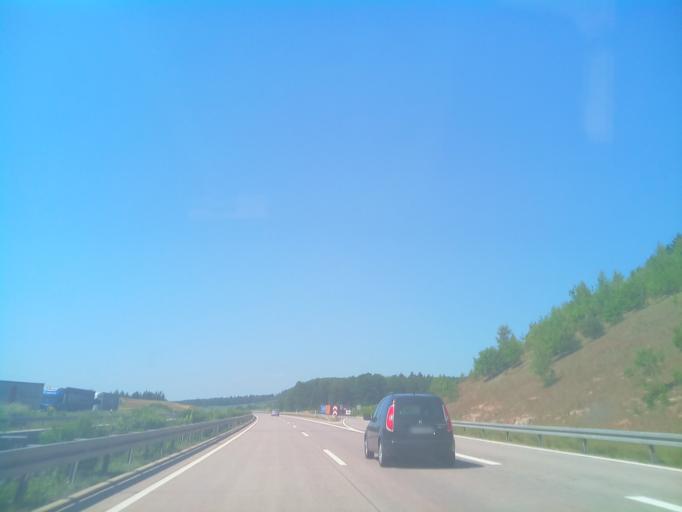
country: DE
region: Thuringia
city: Wolfershausen
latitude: 50.4684
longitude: 10.4538
